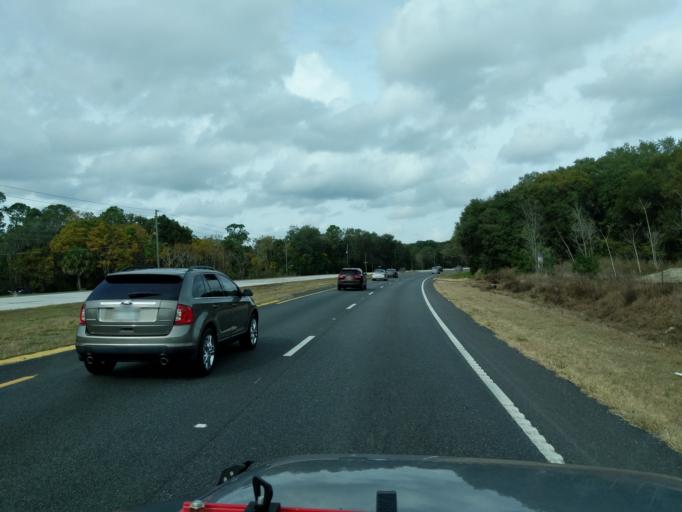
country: US
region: Florida
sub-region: Orange County
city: Tangerine
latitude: 28.7533
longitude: -81.6234
